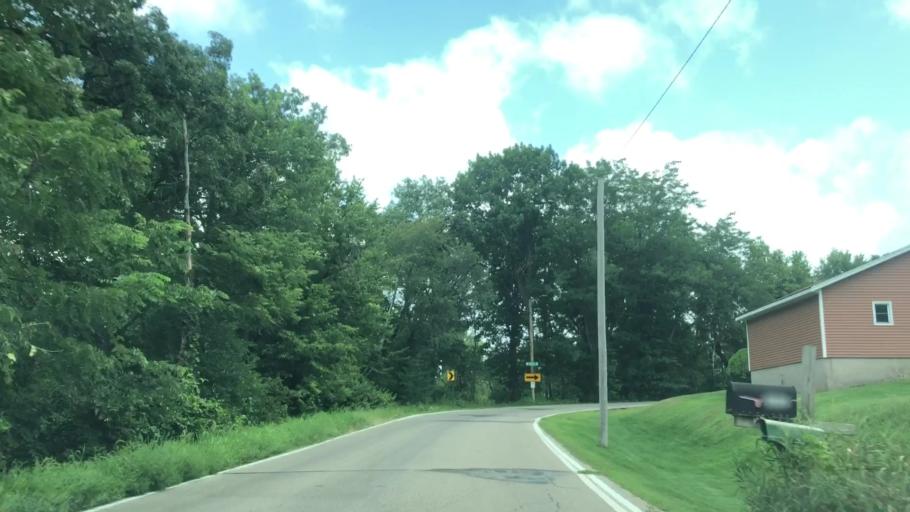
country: US
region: Iowa
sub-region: Marshall County
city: Marshalltown
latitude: 42.0281
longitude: -92.9459
